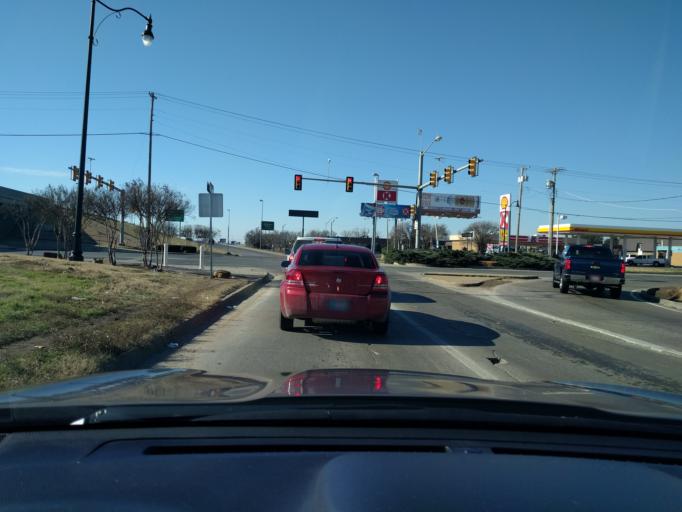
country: US
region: Oklahoma
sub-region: Oklahoma County
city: Warr Acres
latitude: 35.4605
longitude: -97.6007
